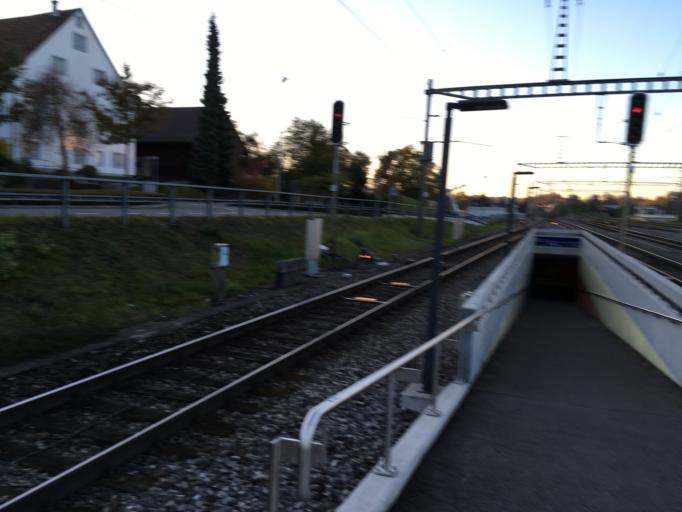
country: CH
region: Zurich
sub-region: Bezirk Hinwil
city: Wetzikon / Unter-Wetzikon
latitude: 47.3185
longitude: 8.7911
